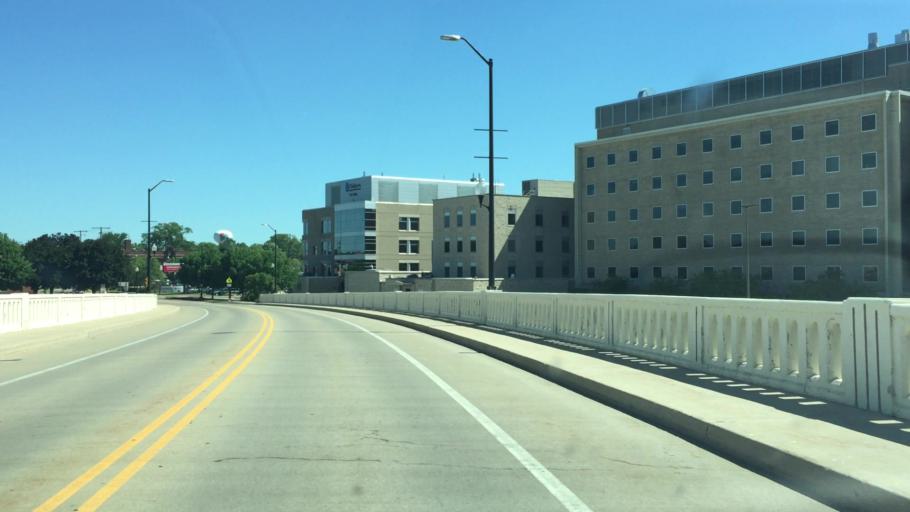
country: US
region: Wisconsin
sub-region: Winnebago County
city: Neenah
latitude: 44.1865
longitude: -88.4554
